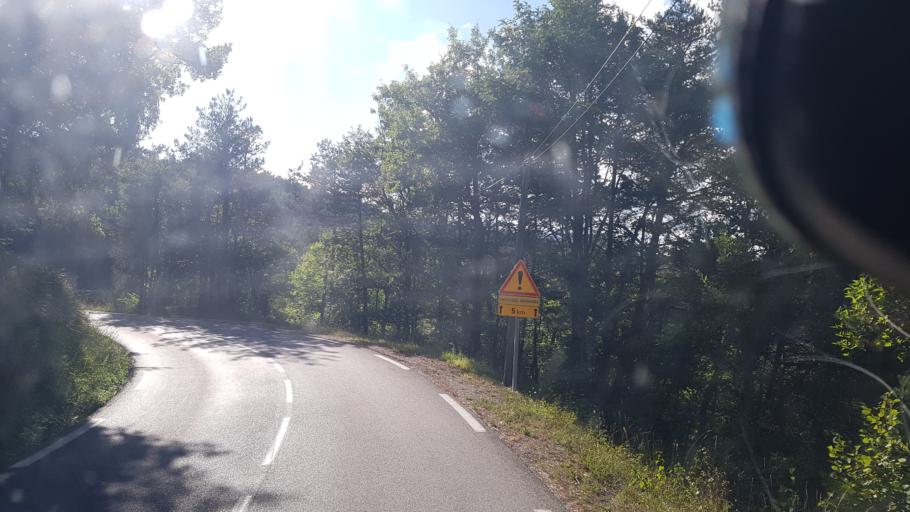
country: FR
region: Rhone-Alpes
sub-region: Departement de l'Isere
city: Mens
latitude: 44.8291
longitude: 5.6571
